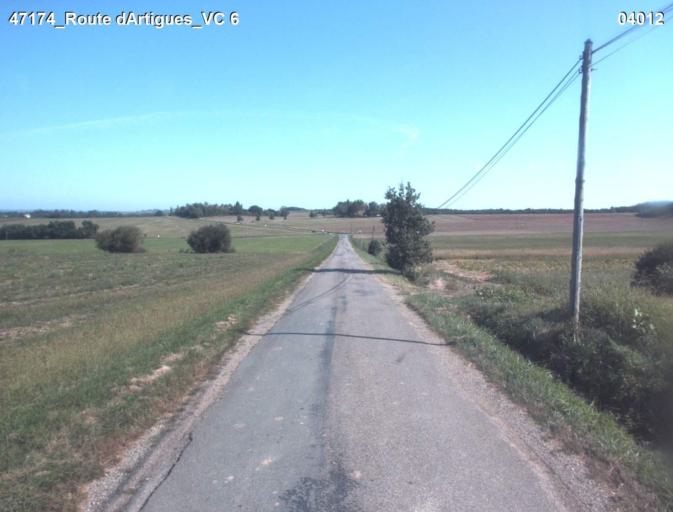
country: FR
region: Aquitaine
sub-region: Departement du Lot-et-Garonne
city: Nerac
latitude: 44.0585
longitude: 0.3360
